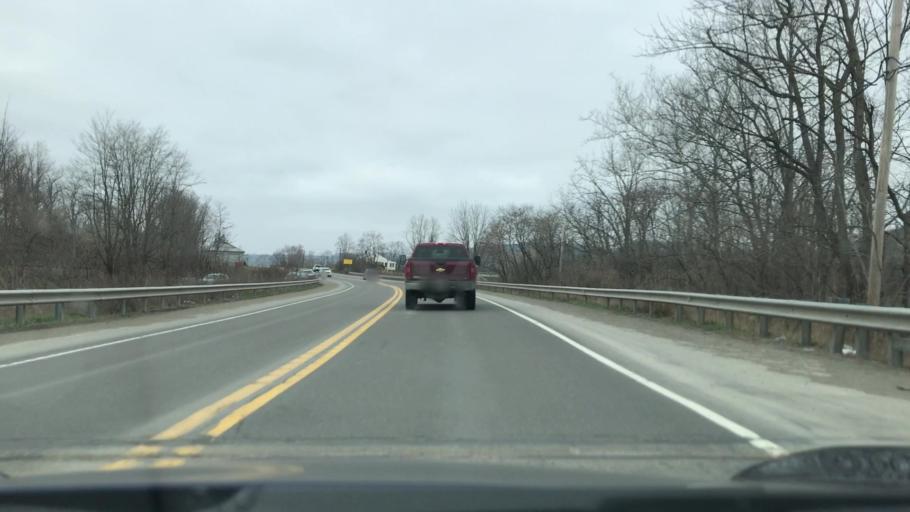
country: US
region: Pennsylvania
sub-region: Bradford County
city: Towanda
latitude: 41.7784
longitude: -76.3861
